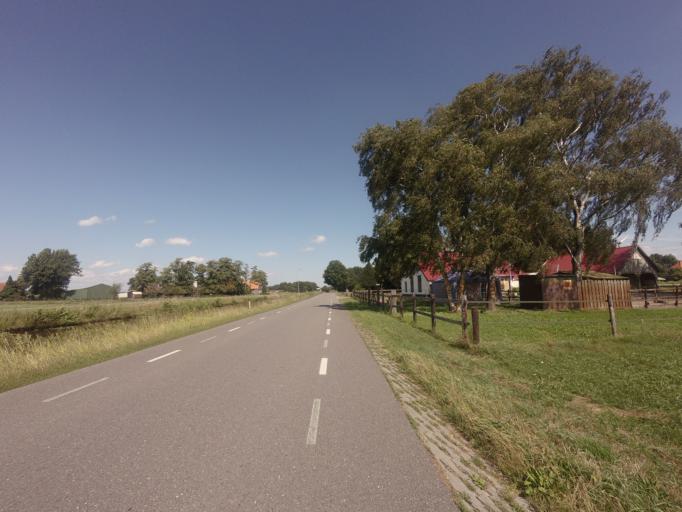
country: NL
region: Overijssel
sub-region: Gemeente Twenterand
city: Den Ham
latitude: 52.5683
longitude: 6.4401
